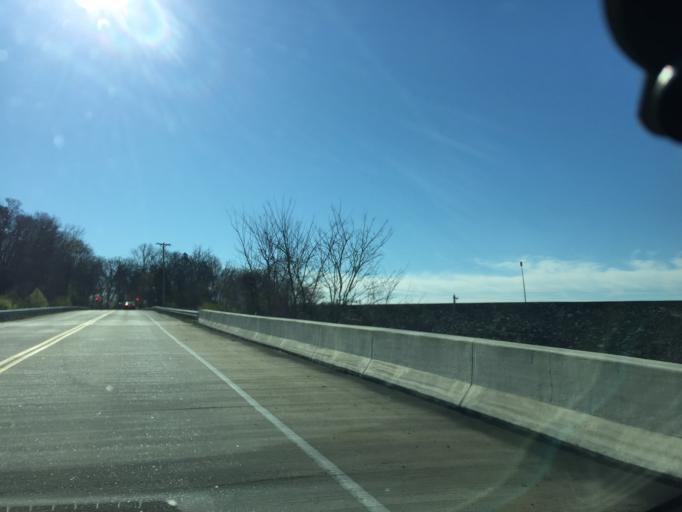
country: US
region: Tennessee
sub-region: Hamilton County
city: East Chattanooga
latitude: 35.1089
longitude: -85.2263
